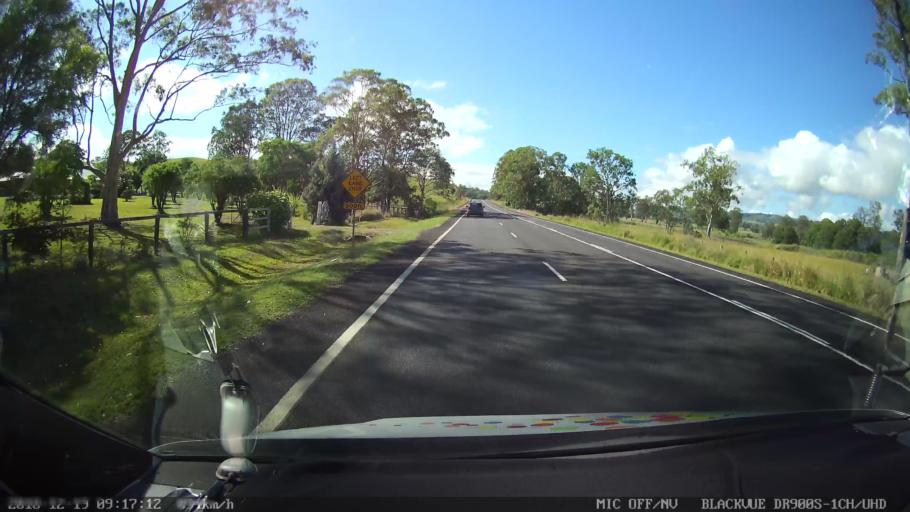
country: AU
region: New South Wales
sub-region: Kyogle
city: Kyogle
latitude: -28.5303
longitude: 152.9729
